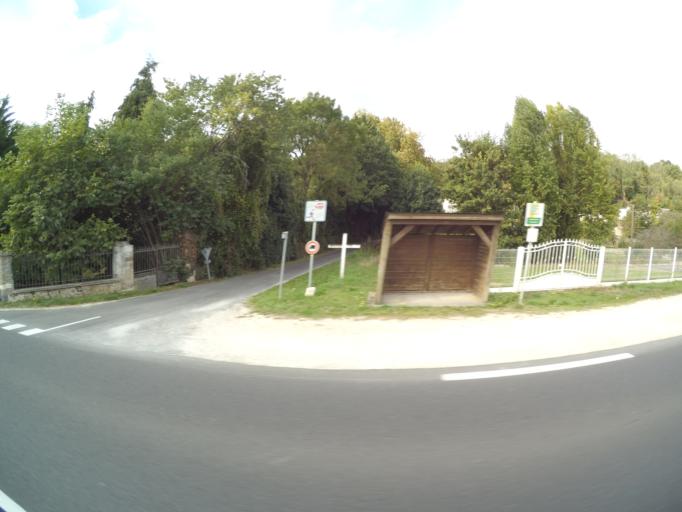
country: FR
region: Centre
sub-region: Departement d'Indre-et-Loire
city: Cinq-Mars-la-Pile
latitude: 47.3543
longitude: 0.4825
